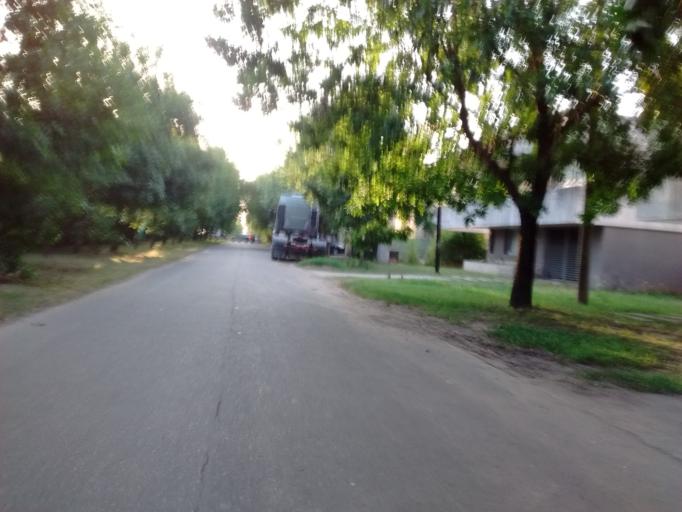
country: AR
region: Santa Fe
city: Funes
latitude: -32.9160
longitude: -60.7538
